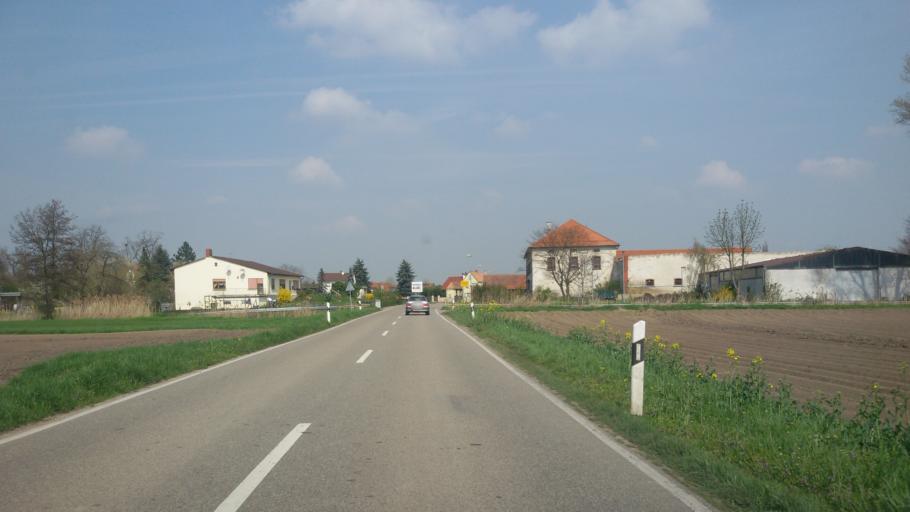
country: DE
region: Rheinland-Pfalz
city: Gerolsheim
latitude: 49.5614
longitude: 8.2612
